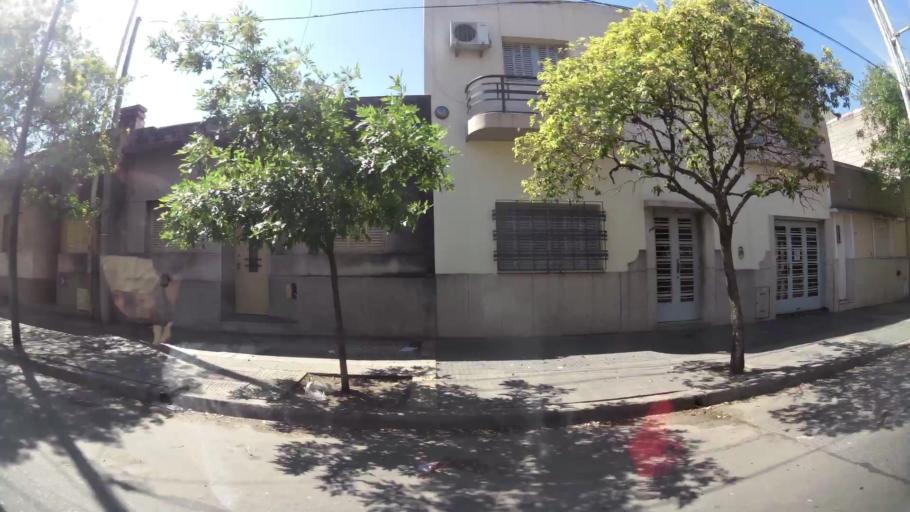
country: AR
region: Cordoba
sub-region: Departamento de Capital
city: Cordoba
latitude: -31.4102
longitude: -64.1657
